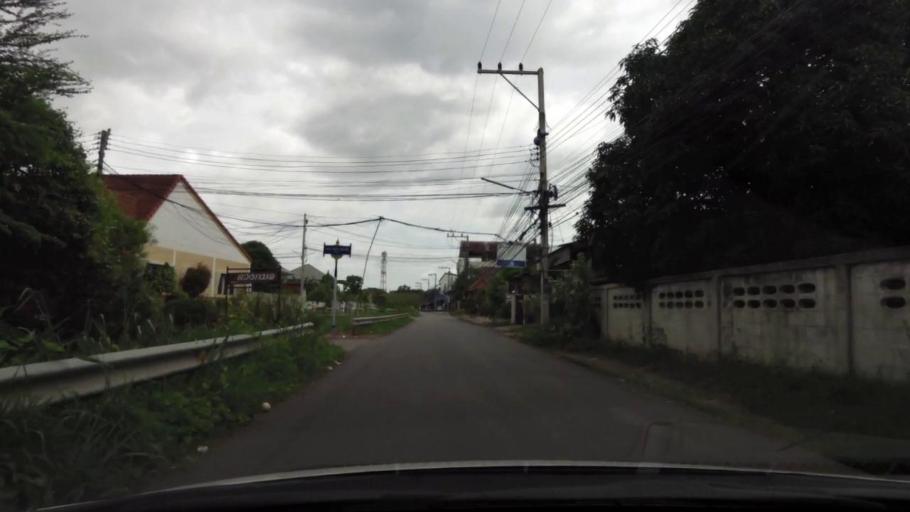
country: TH
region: Ratchaburi
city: Ratchaburi
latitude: 13.5294
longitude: 99.8326
